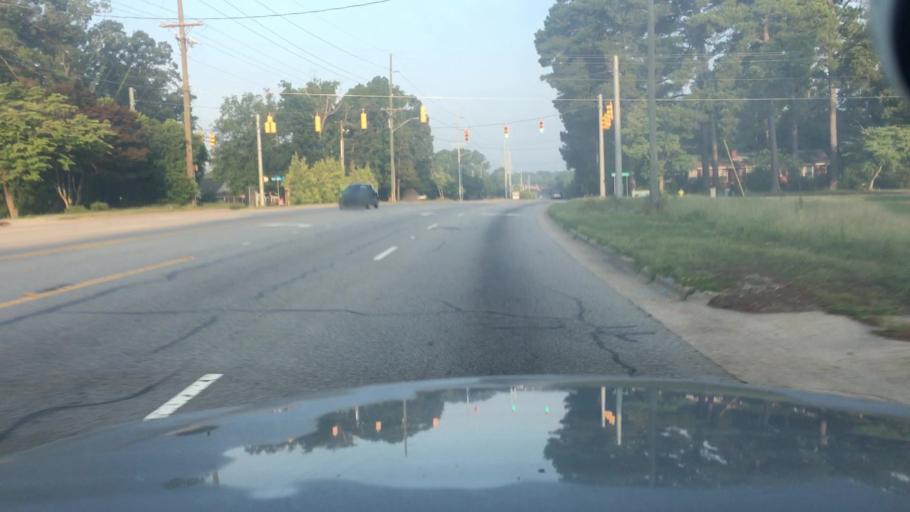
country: US
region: North Carolina
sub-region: Cumberland County
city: Fayetteville
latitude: 35.1044
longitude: -78.8859
